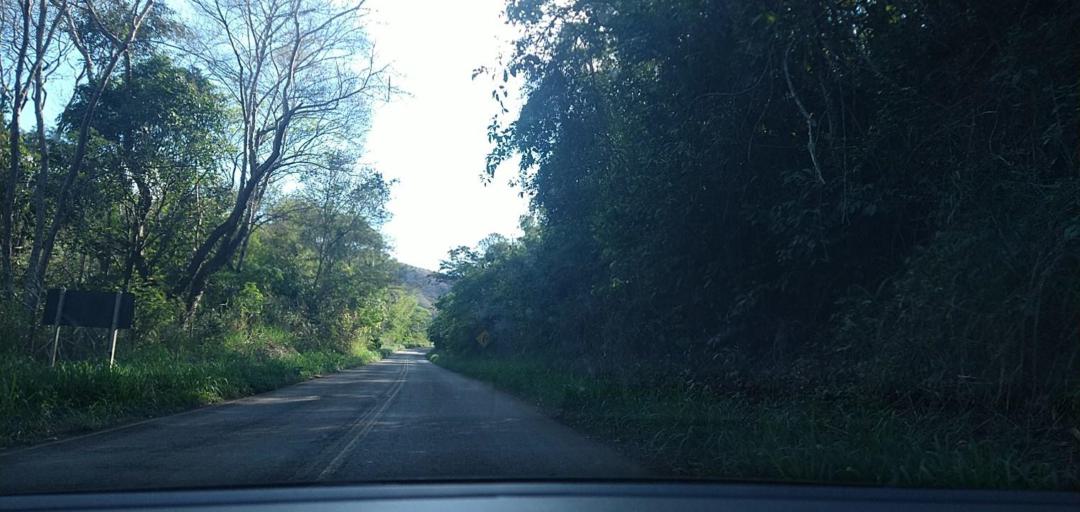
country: BR
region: Minas Gerais
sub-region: Alvinopolis
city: Alvinopolis
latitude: -20.1734
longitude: -42.9226
